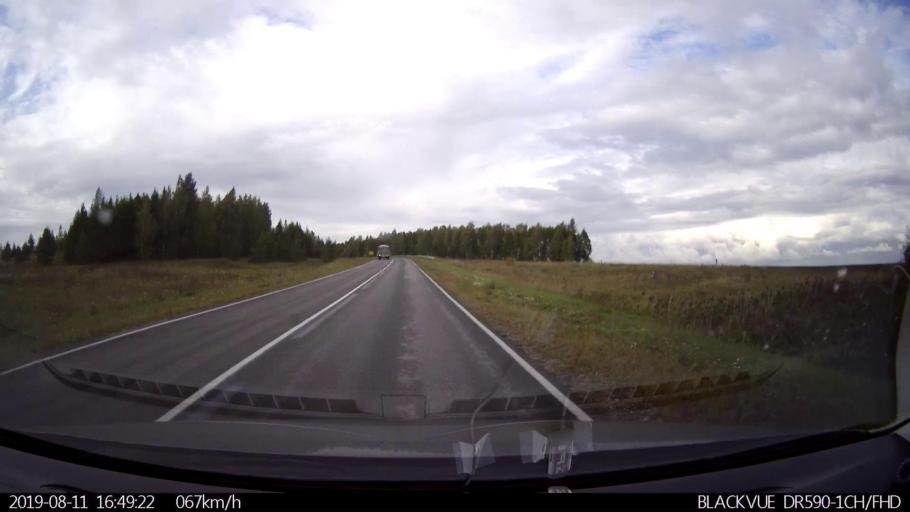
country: RU
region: Ulyanovsk
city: Mayna
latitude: 54.2201
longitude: 47.6957
